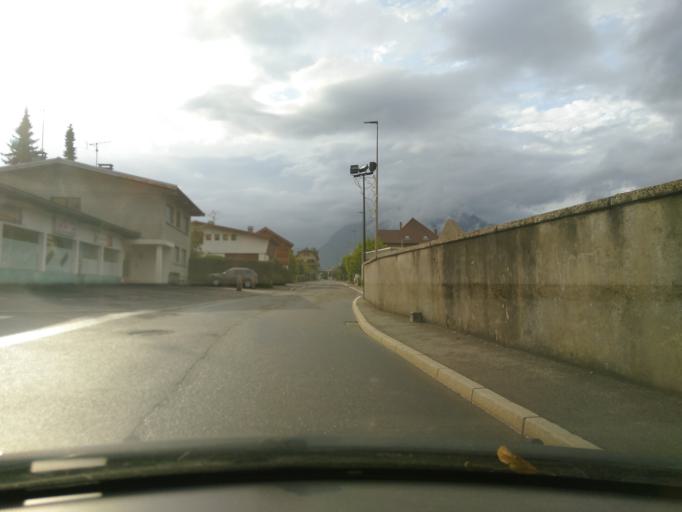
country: FR
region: Rhone-Alpes
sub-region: Departement de la Haute-Savoie
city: Marnaz
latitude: 46.0589
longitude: 6.5343
